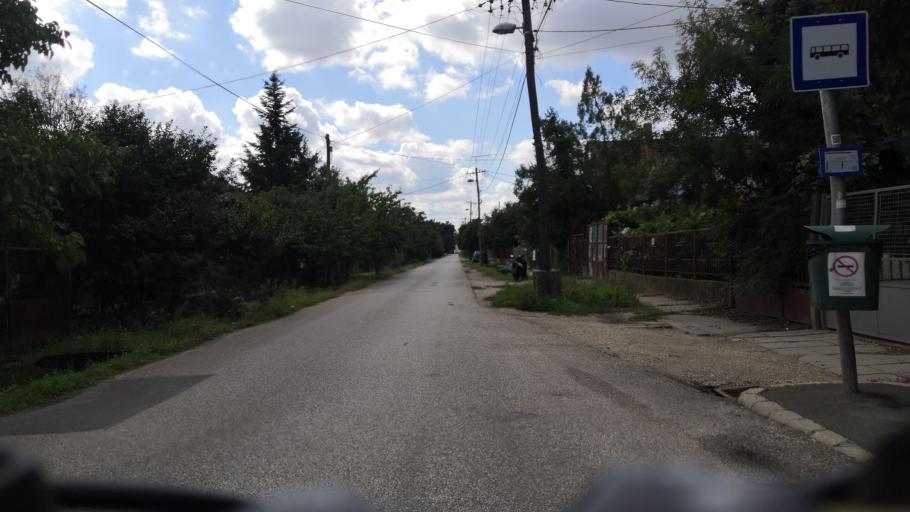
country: HU
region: Csongrad
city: Szeged
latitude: 46.2783
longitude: 20.1204
